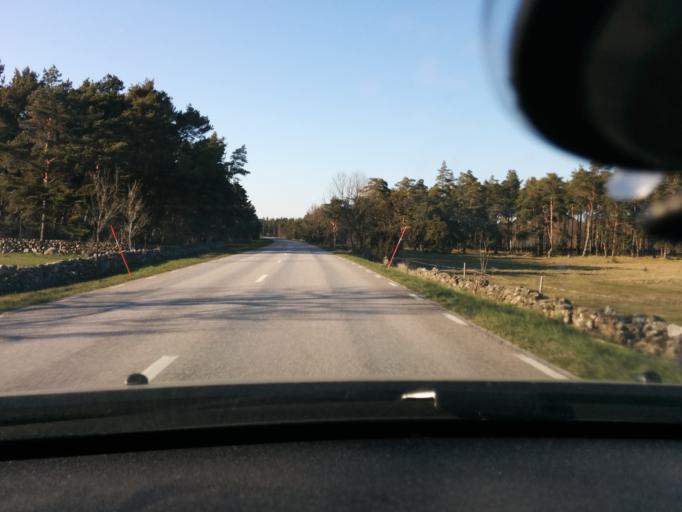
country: SE
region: Gotland
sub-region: Gotland
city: Hemse
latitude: 57.1406
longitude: 18.3483
